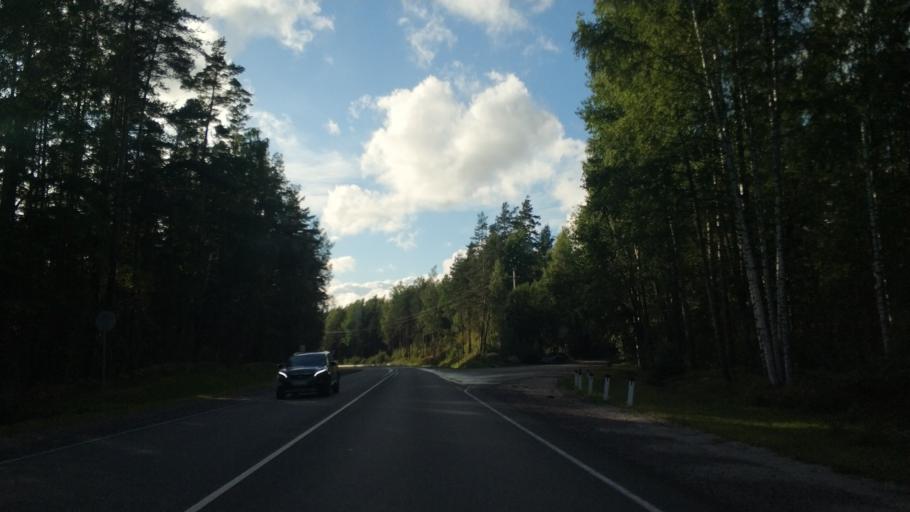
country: RU
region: Leningrad
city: Sapernoye
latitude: 60.7148
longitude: 30.0134
